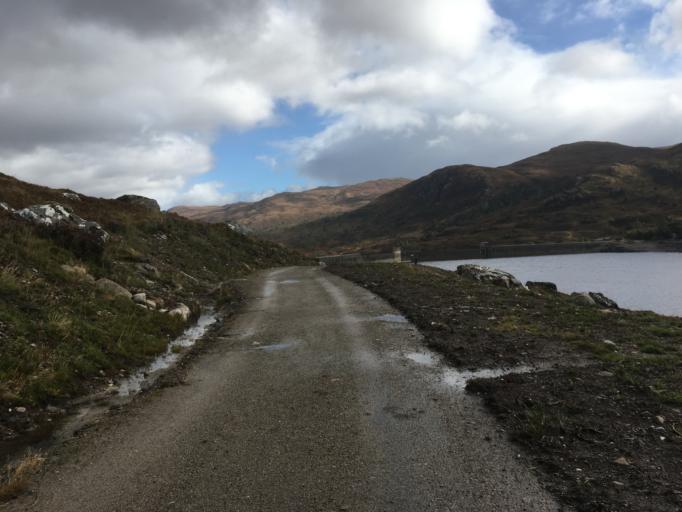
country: GB
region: Scotland
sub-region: Highland
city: Spean Bridge
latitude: 57.3398
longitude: -4.9665
